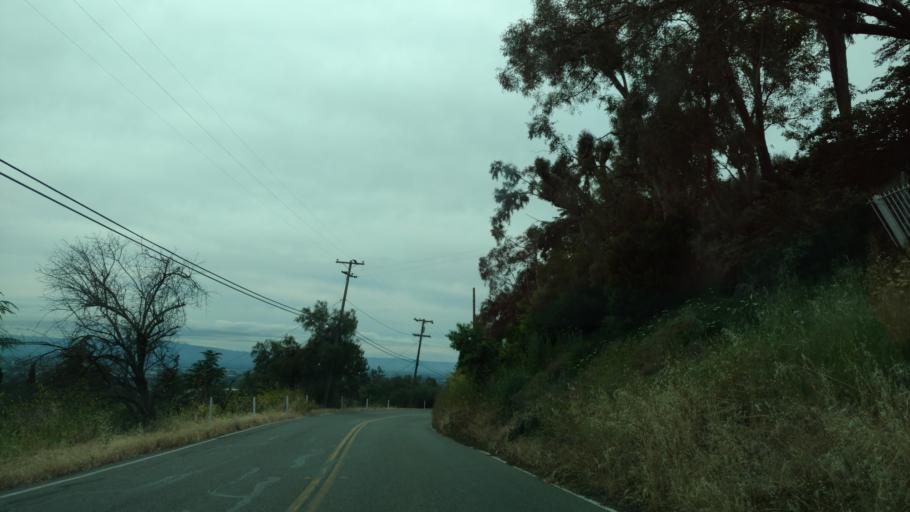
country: US
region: California
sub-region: Santa Clara County
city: East Foothills
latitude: 37.3802
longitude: -121.8114
